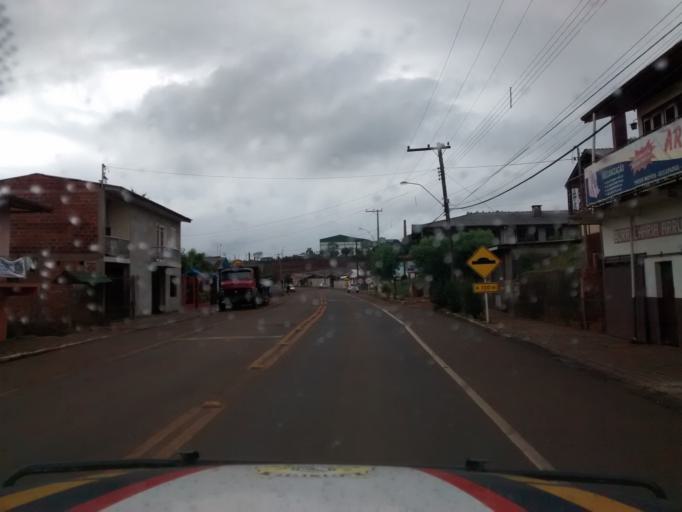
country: BR
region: Rio Grande do Sul
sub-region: Lagoa Vermelha
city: Lagoa Vermelha
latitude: -28.2022
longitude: -51.5253
